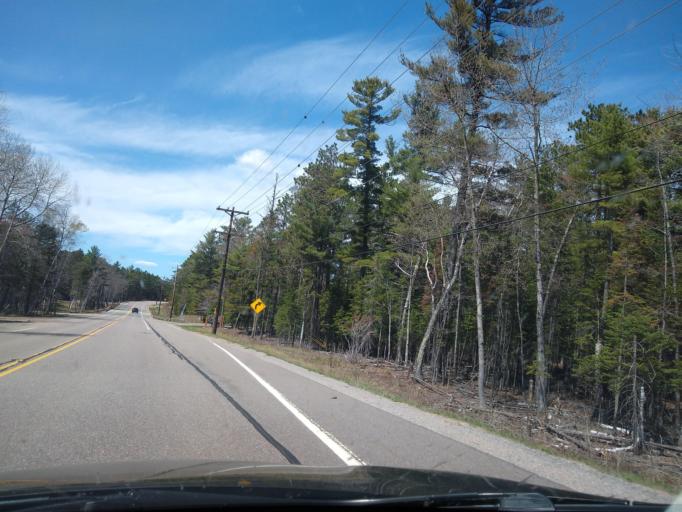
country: US
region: Michigan
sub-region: Marquette County
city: Trowbridge Park
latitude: 46.6318
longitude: -87.4732
